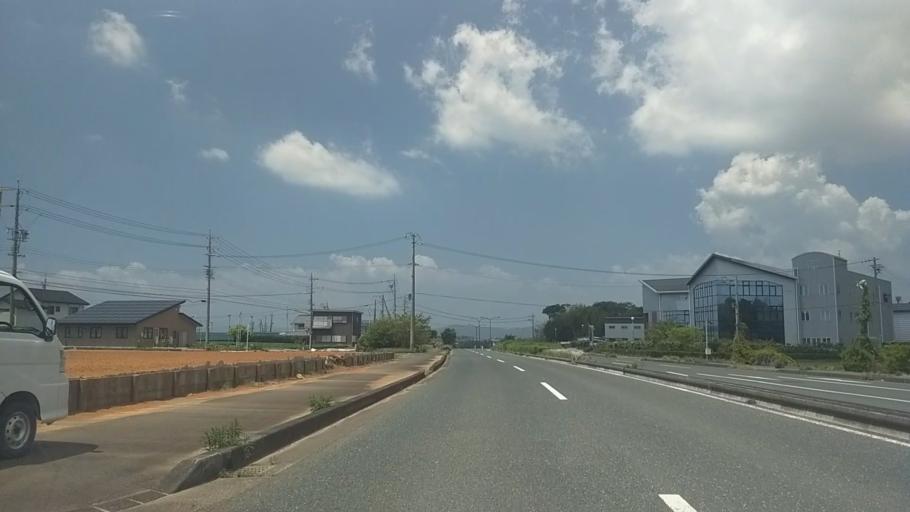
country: JP
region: Shizuoka
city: Hamamatsu
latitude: 34.7694
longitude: 137.6875
